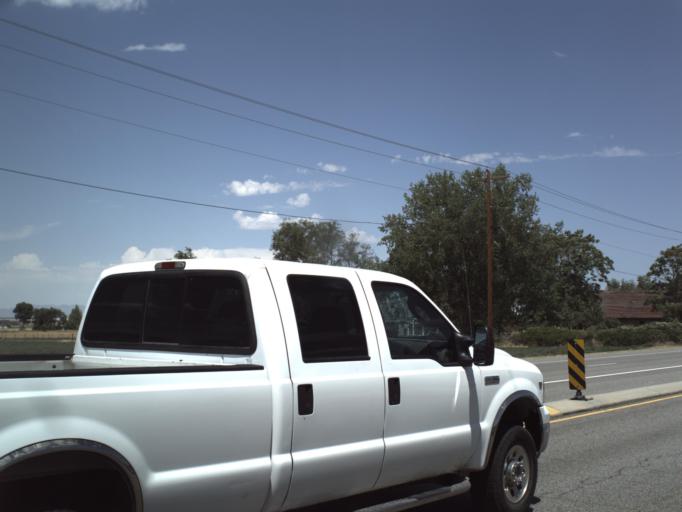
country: US
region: Utah
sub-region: Tooele County
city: Erda
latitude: 40.6061
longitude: -112.2942
